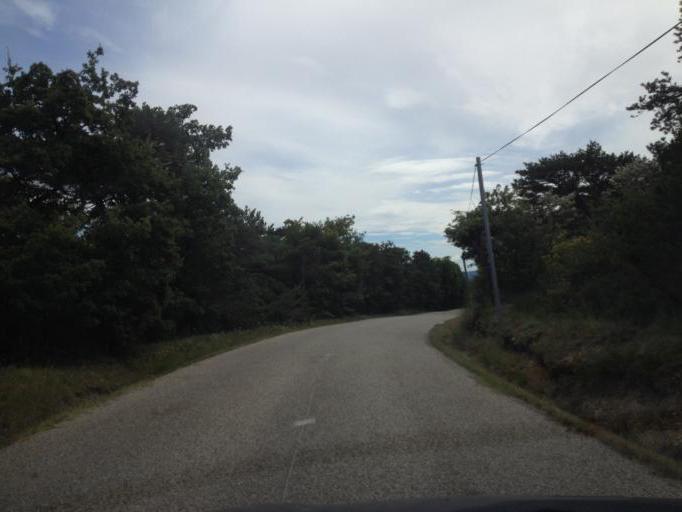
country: FR
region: Rhone-Alpes
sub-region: Departement de la Drome
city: Allan
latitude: 44.4726
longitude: 4.8230
